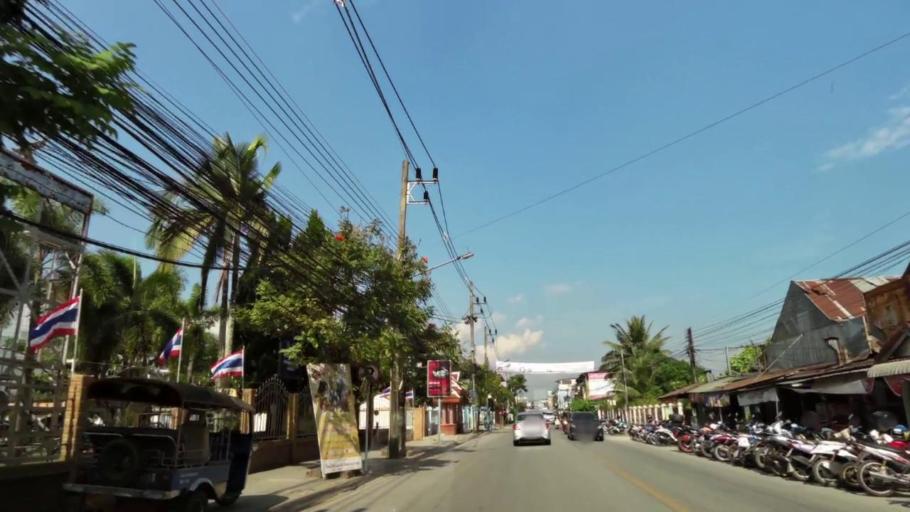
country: TH
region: Chiang Rai
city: Chiang Rai
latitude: 19.9032
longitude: 99.8283
